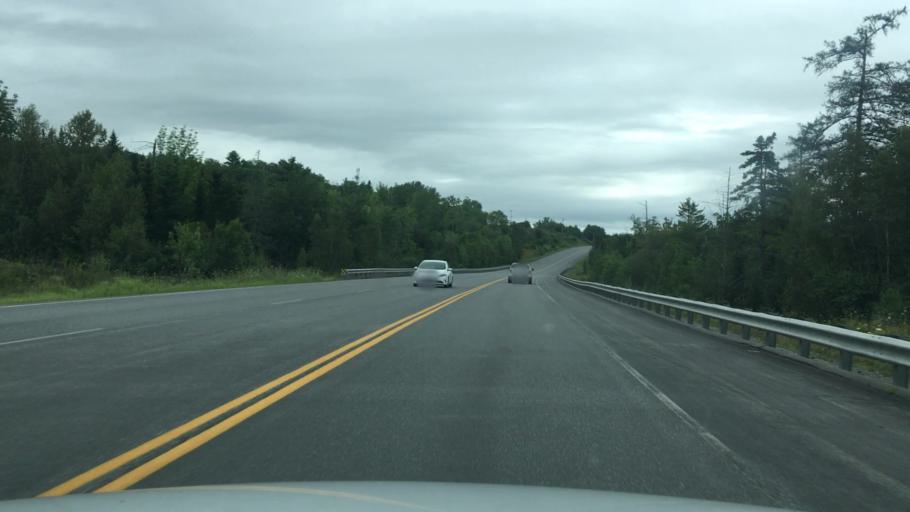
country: US
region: Maine
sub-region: Hancock County
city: Franklin
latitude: 44.8560
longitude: -68.3229
